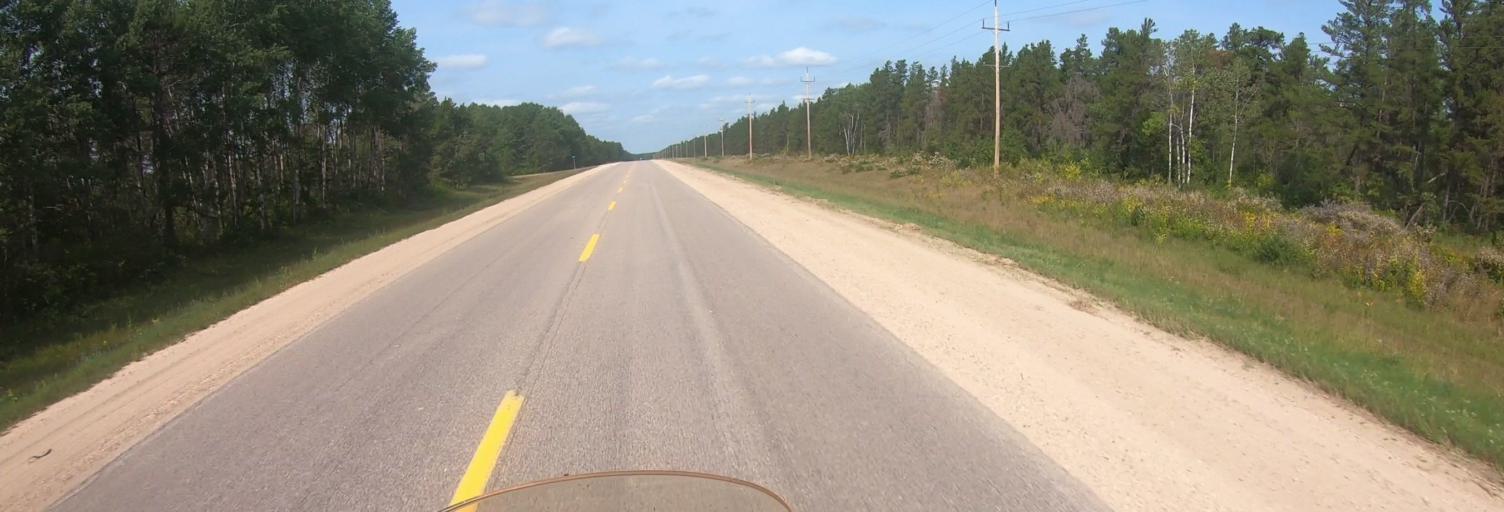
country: CA
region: Manitoba
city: La Broquerie
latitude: 49.1771
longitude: -96.1787
